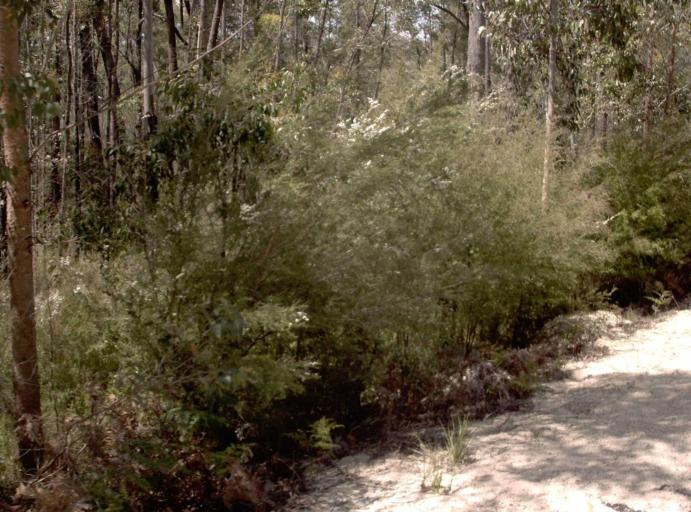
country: AU
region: New South Wales
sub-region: Bombala
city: Bombala
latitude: -37.5669
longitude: 149.1946
